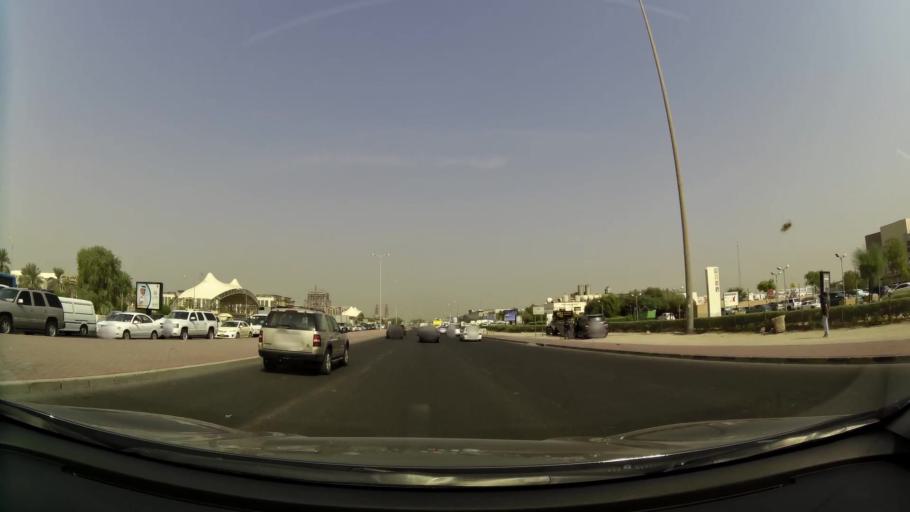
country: KW
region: Al Asimah
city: Ar Rabiyah
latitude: 29.3019
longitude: 47.9275
